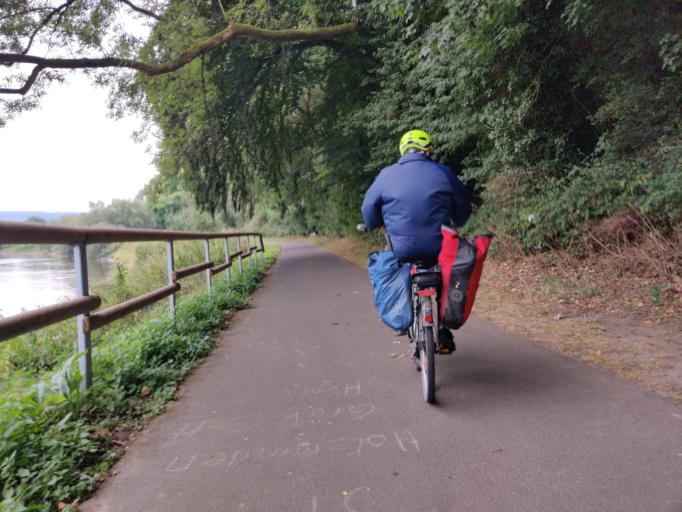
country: DE
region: North Rhine-Westphalia
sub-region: Regierungsbezirk Detmold
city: Hoexter
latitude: 51.8050
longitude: 9.4035
